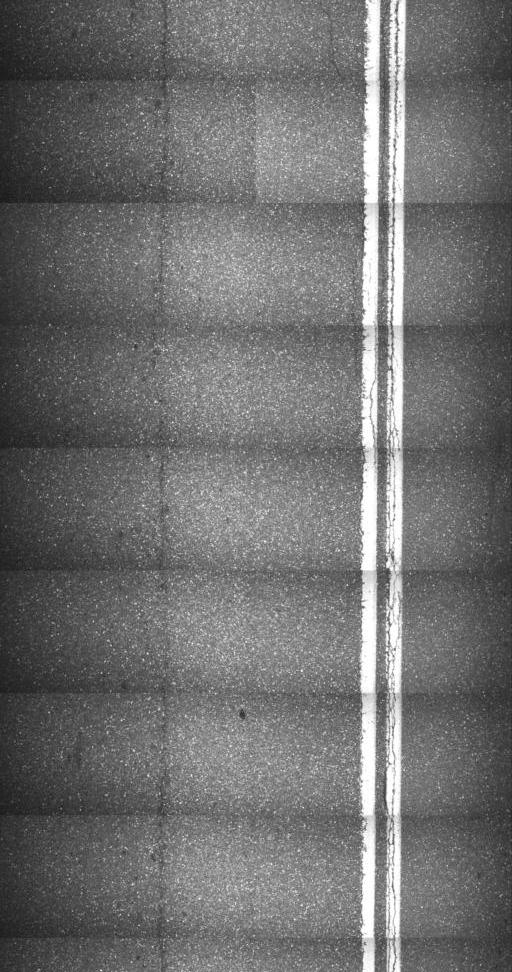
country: US
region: Vermont
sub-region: Orange County
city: Randolph
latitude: 43.8318
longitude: -72.7933
